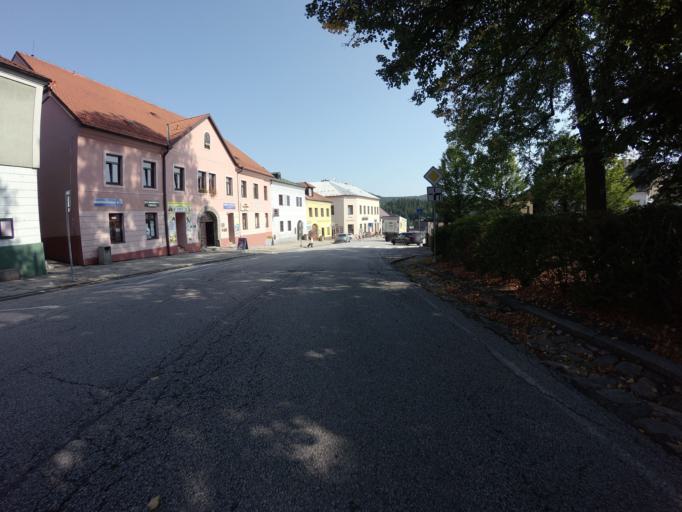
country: CZ
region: Jihocesky
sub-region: Okres Cesky Krumlov
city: Vyssi Brod
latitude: 48.6160
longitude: 14.3120
